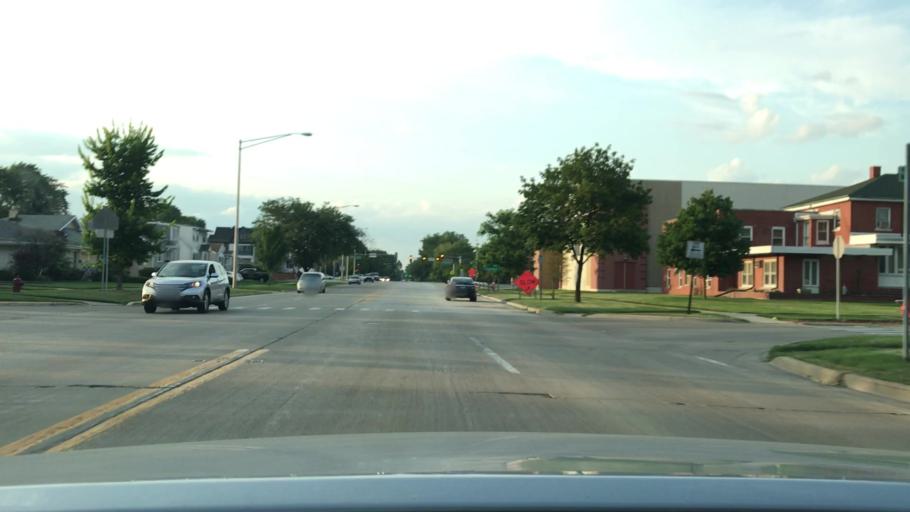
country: US
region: Illinois
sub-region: Cook County
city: Oak Lawn
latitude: 41.7214
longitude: -87.7603
